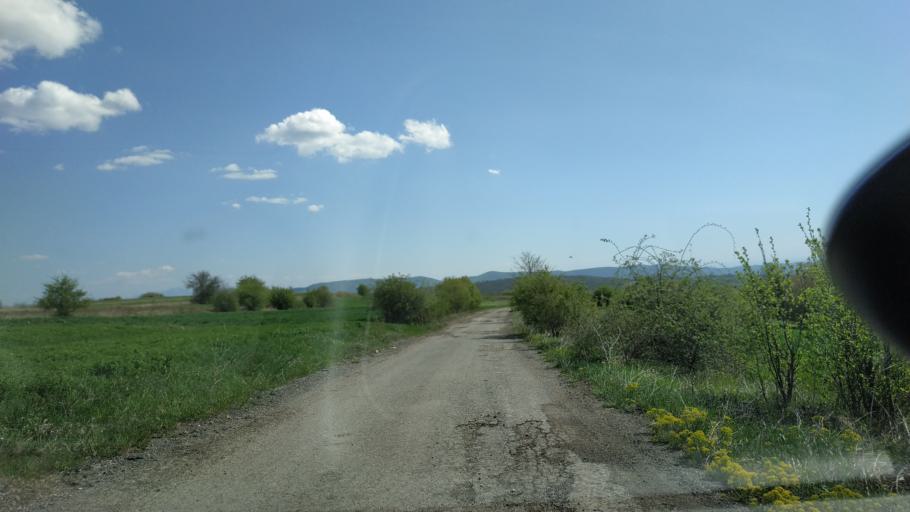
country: RS
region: Central Serbia
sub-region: Zajecarski Okrug
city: Soko Banja
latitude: 43.5268
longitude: 21.9062
